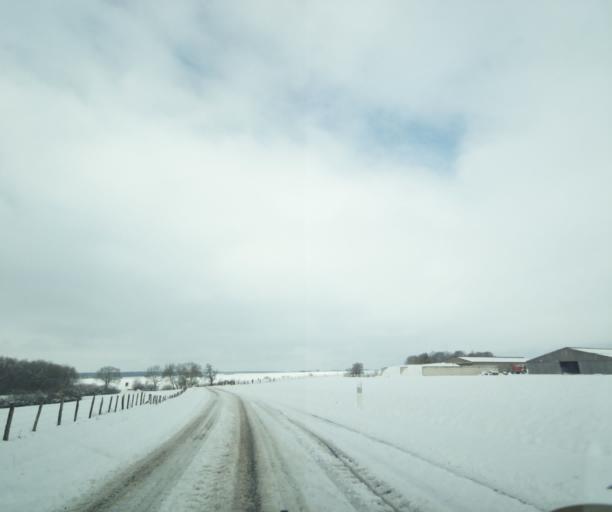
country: FR
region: Champagne-Ardenne
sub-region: Departement de la Haute-Marne
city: Montier-en-Der
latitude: 48.5189
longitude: 4.6783
